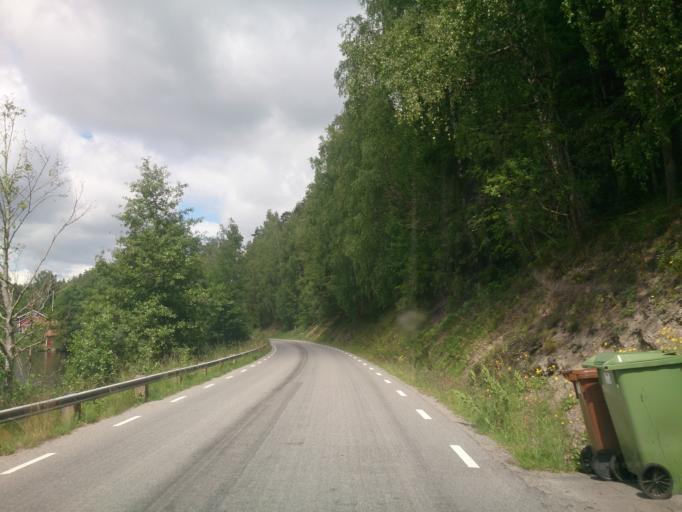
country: SE
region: OEstergoetland
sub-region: Norrkopings Kommun
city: Jursla
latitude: 58.7168
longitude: 16.1553
